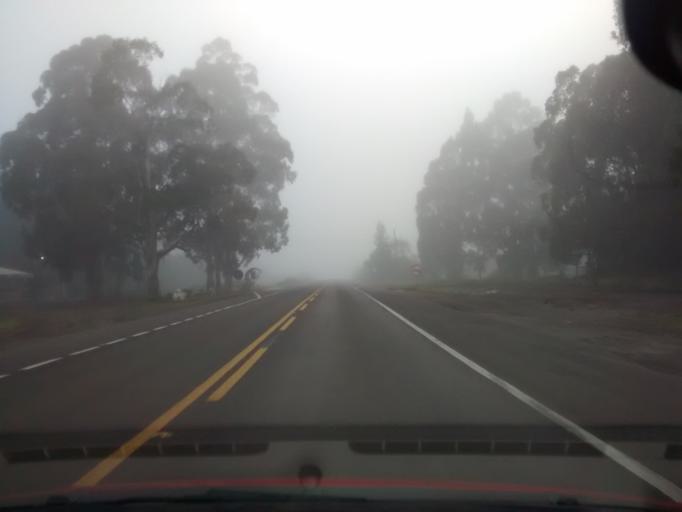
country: BR
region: Rio Grande do Sul
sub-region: Vacaria
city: Vacaria
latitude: -28.2995
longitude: -50.8038
